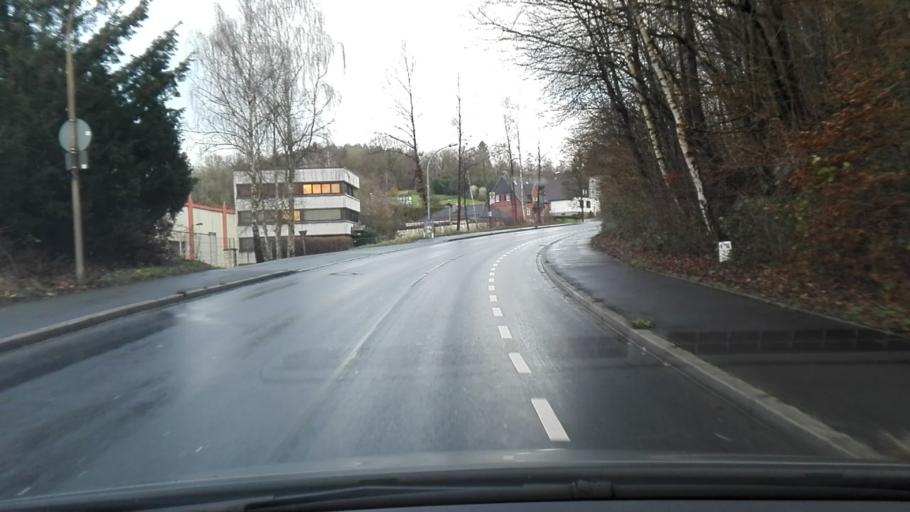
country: DE
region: North Rhine-Westphalia
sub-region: Regierungsbezirk Arnsberg
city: Frondenberg
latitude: 51.4760
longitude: 7.7777
